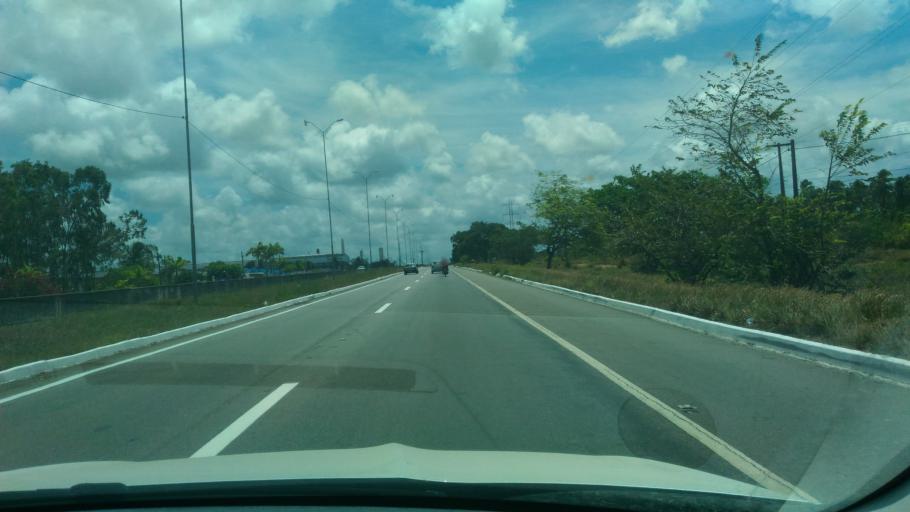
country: BR
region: Paraiba
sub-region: Conde
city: Conde
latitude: -7.2446
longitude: -34.9302
